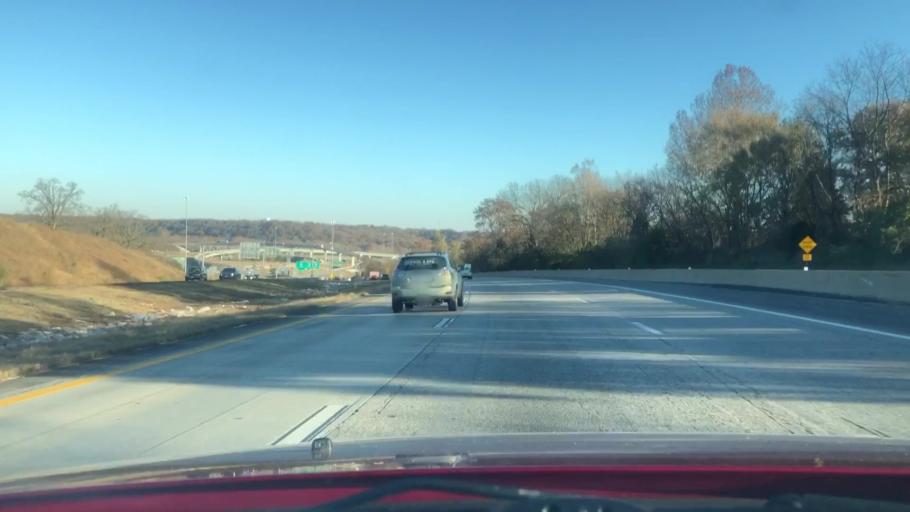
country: US
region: Missouri
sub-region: Greene County
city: Springfield
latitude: 37.1316
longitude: -93.2432
